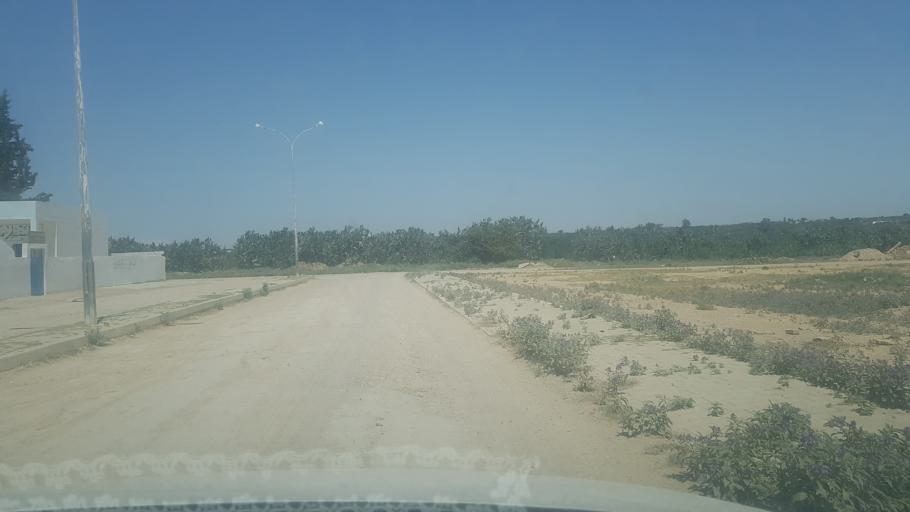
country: TN
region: Al Qayrawan
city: Kairouan
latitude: 35.6235
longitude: 9.9246
